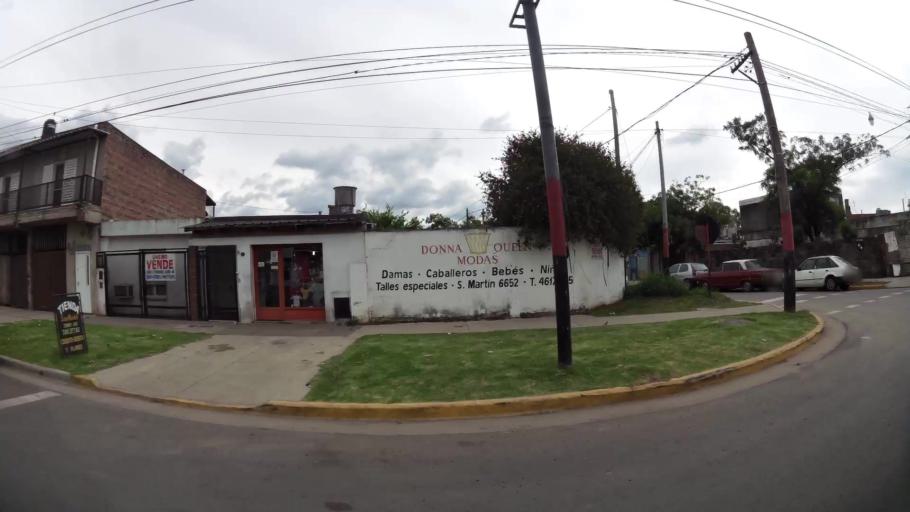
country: AR
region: Santa Fe
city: Gobernador Galvez
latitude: -33.0145
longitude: -60.6519
